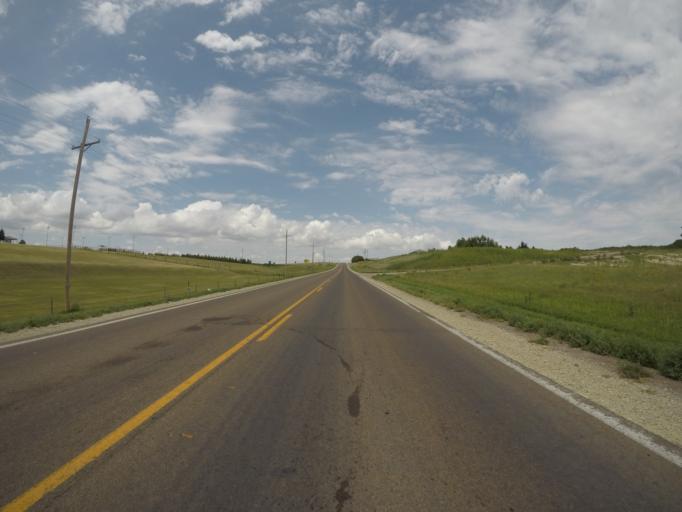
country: US
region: Kansas
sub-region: Rawlins County
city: Atwood
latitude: 39.8260
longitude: -101.0468
